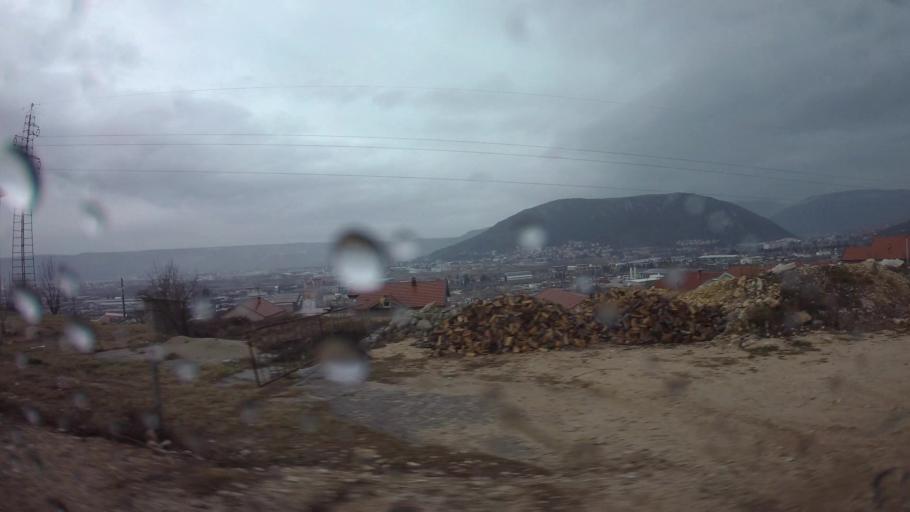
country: BA
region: Federation of Bosnia and Herzegovina
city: Rodoc
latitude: 43.3133
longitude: 17.8377
